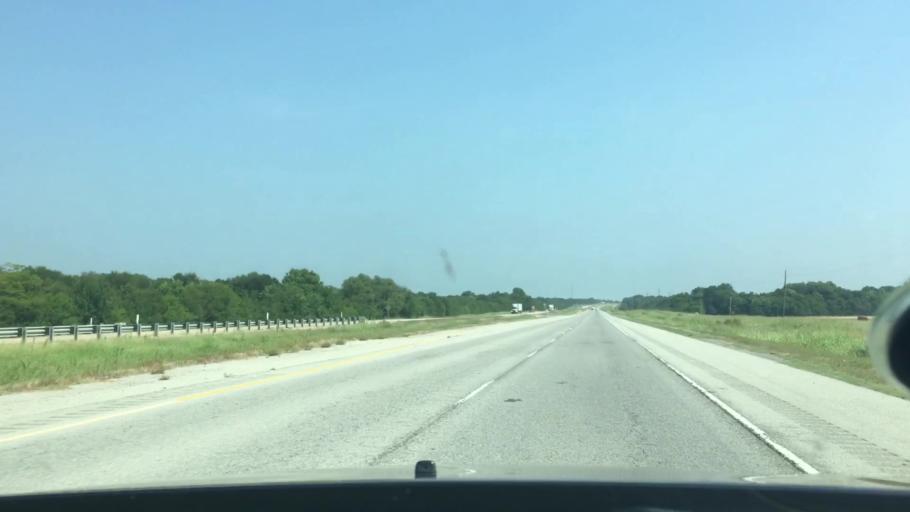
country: US
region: Oklahoma
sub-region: Atoka County
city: Atoka
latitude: 34.2493
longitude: -96.2157
